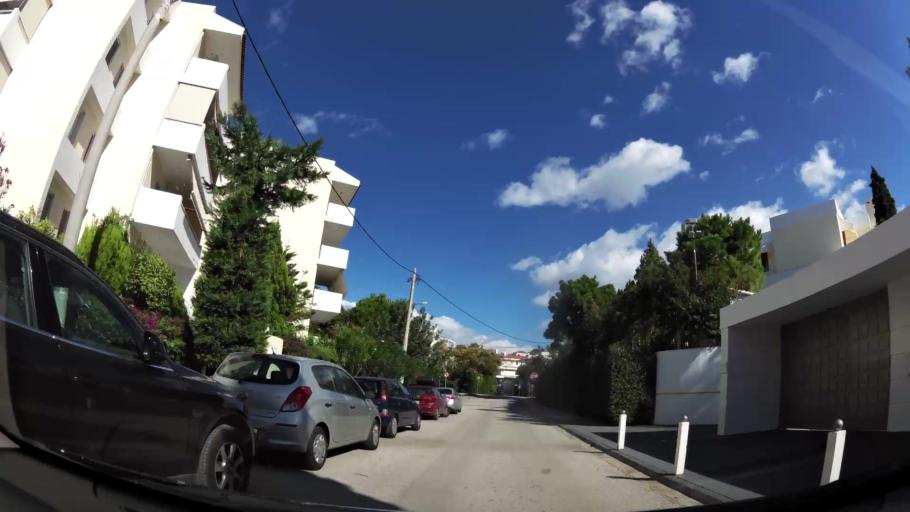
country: GR
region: Attica
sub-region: Nomarchia Anatolikis Attikis
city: Vouliagmeni
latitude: 37.8268
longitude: 23.7777
